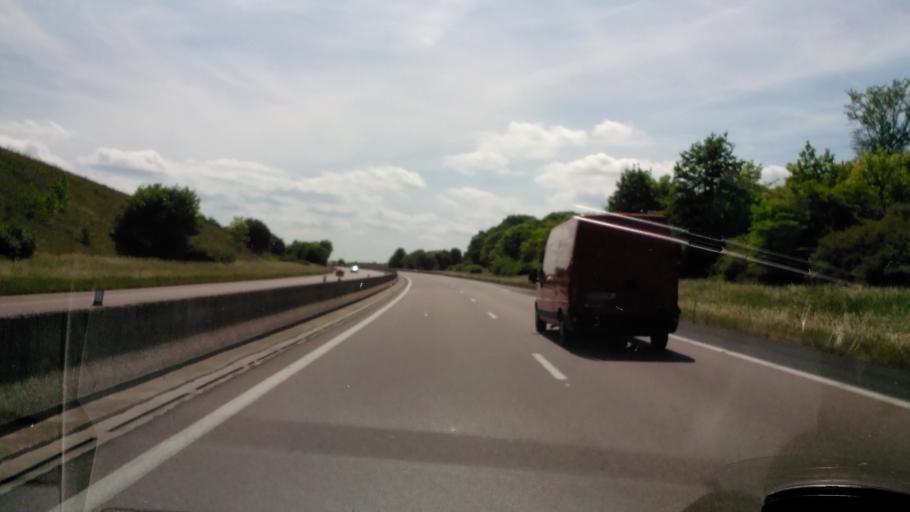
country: FR
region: Lorraine
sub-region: Departement des Vosges
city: Chatenois
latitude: 48.4091
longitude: 5.8691
